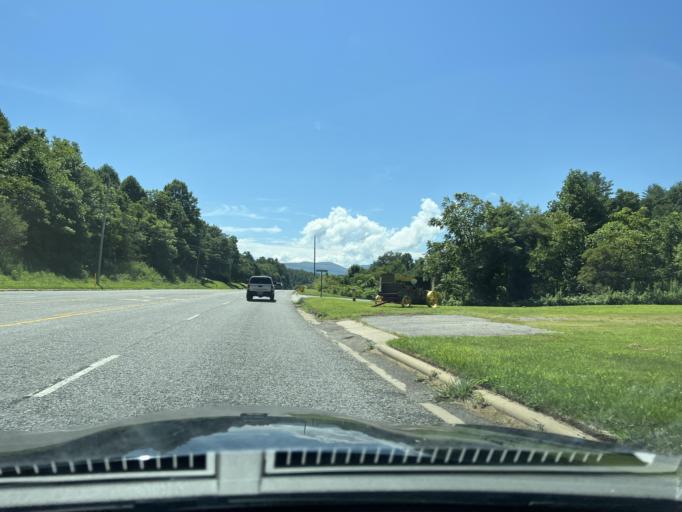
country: US
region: North Carolina
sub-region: Buncombe County
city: Fairview
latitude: 35.5340
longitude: -82.4316
